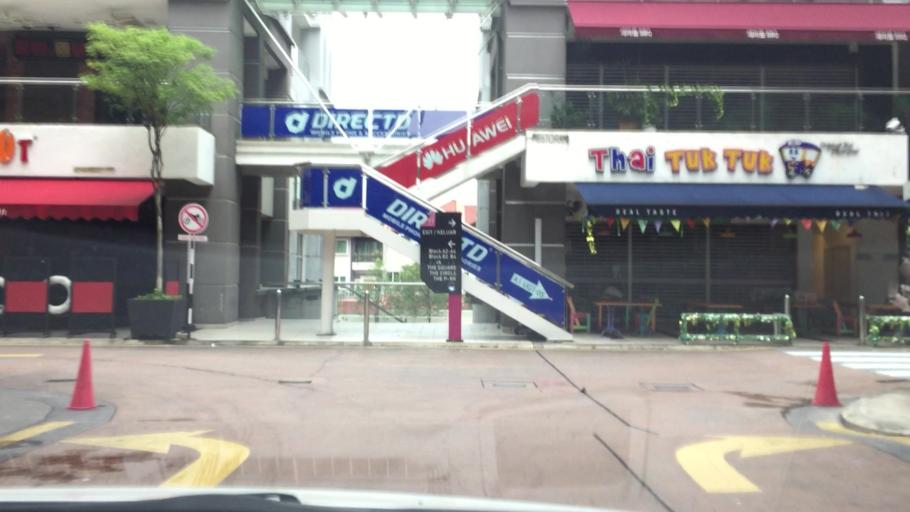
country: MY
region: Kuala Lumpur
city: Kuala Lumpur
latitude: 3.1711
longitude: 101.6648
